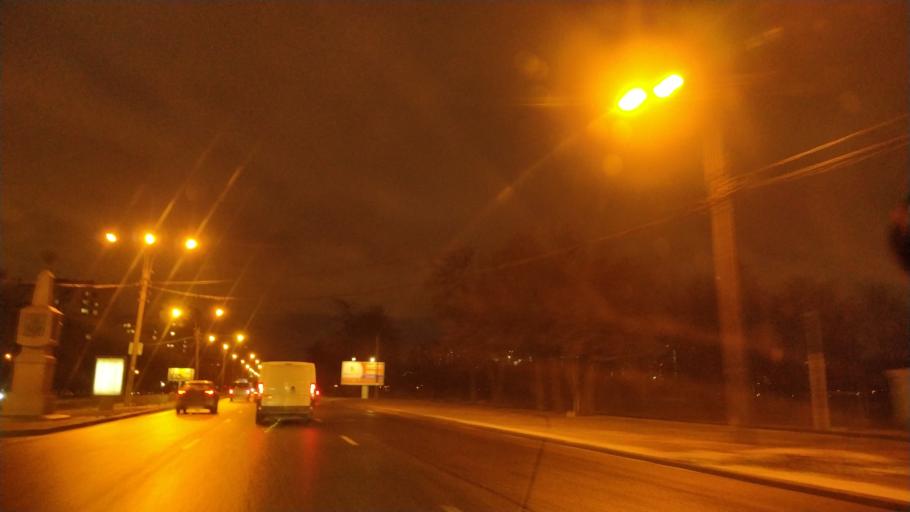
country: RU
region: St.-Petersburg
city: Kupchino
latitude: 59.8411
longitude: 30.3252
